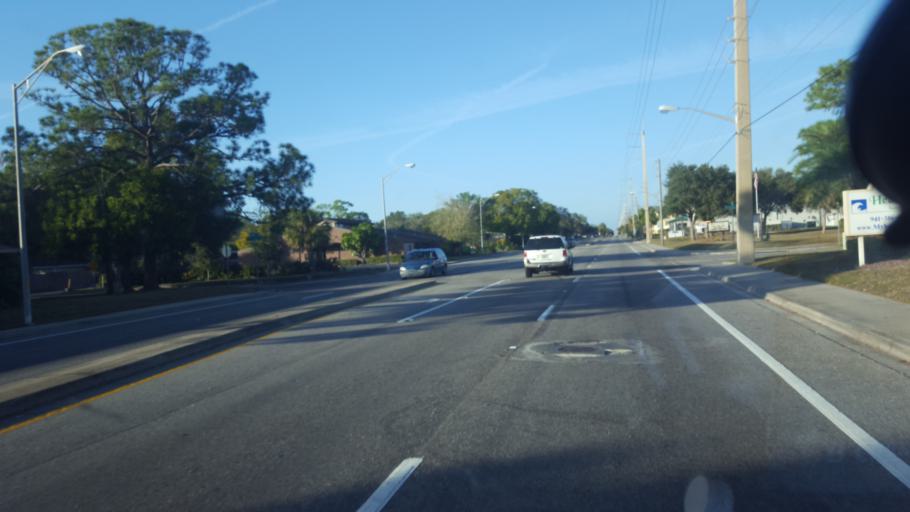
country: US
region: Florida
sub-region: Sarasota County
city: Southgate
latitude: 27.3159
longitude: -82.5140
